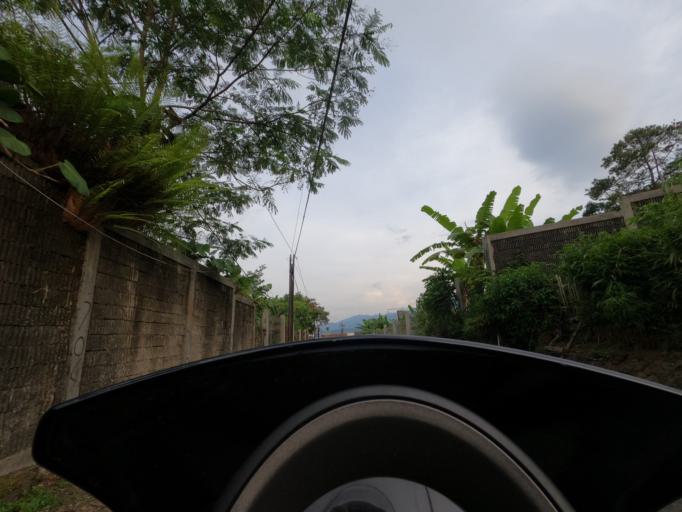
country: ID
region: West Java
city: Lembang
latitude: -6.7334
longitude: 107.6510
